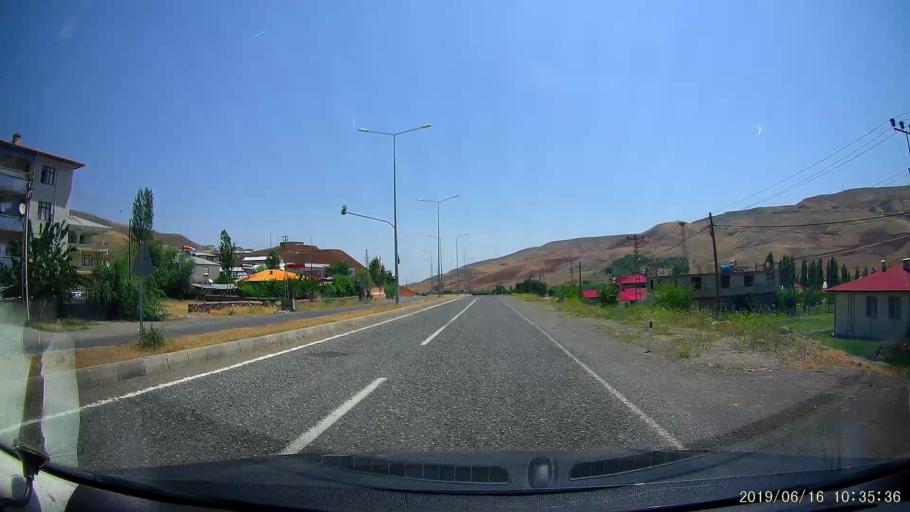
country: TR
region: Igdir
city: Tuzluca
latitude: 40.0357
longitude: 43.6725
